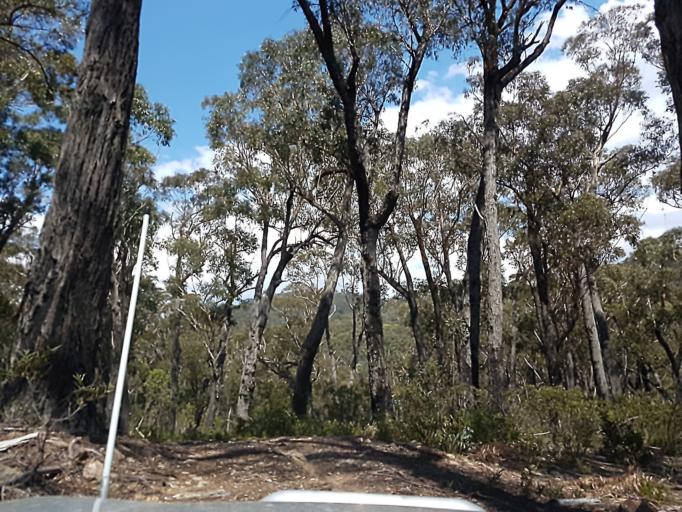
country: AU
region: Victoria
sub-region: East Gippsland
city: Lakes Entrance
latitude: -37.3125
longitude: 148.3457
